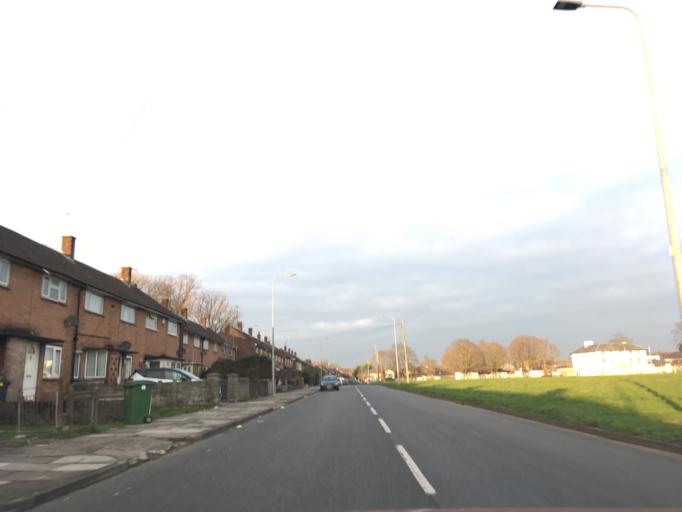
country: GB
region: Wales
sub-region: Newport
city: Marshfield
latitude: 51.5205
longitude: -3.1321
